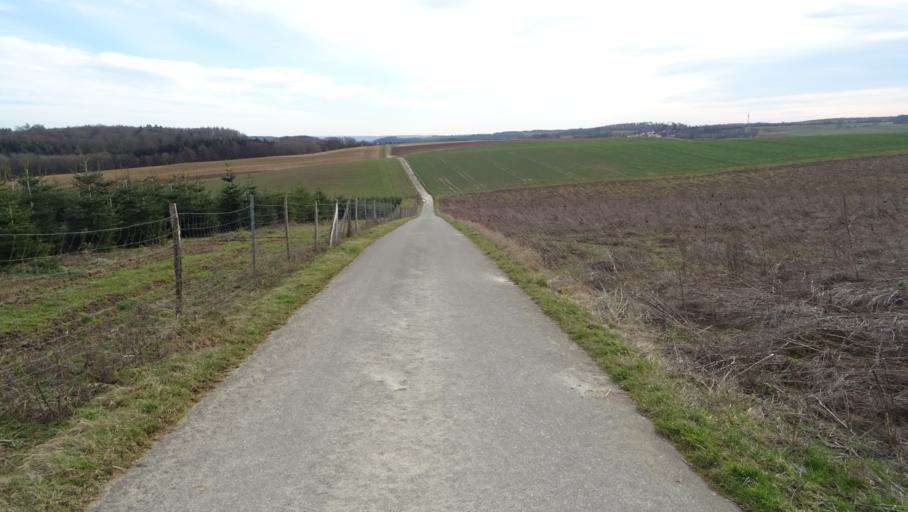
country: DE
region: Baden-Wuerttemberg
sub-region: Karlsruhe Region
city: Billigheim
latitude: 49.3665
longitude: 9.2200
